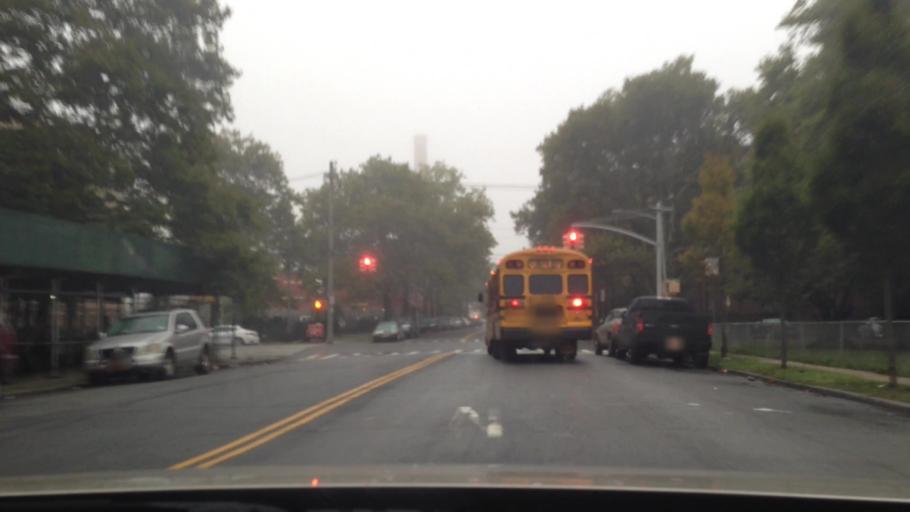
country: US
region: New York
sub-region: Kings County
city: East New York
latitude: 40.6579
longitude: -73.8816
